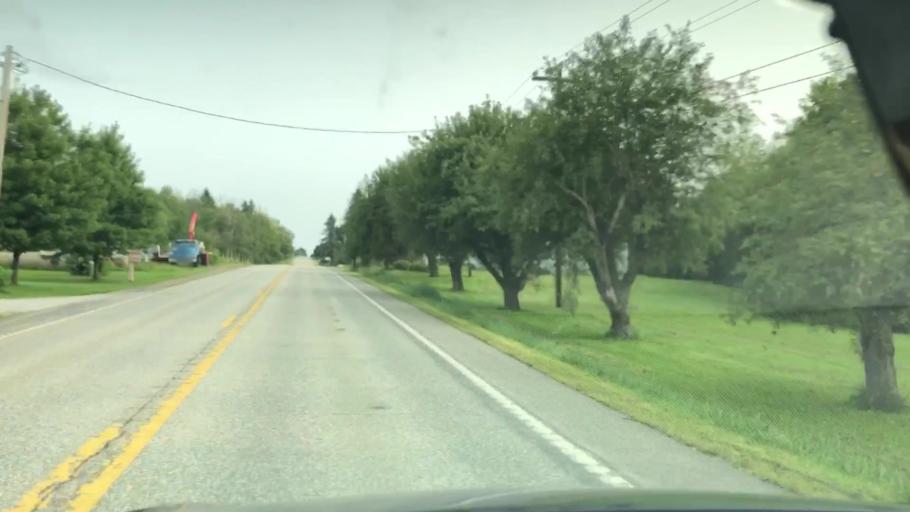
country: US
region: Pennsylvania
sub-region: Erie County
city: Union City
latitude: 41.8800
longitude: -79.8429
